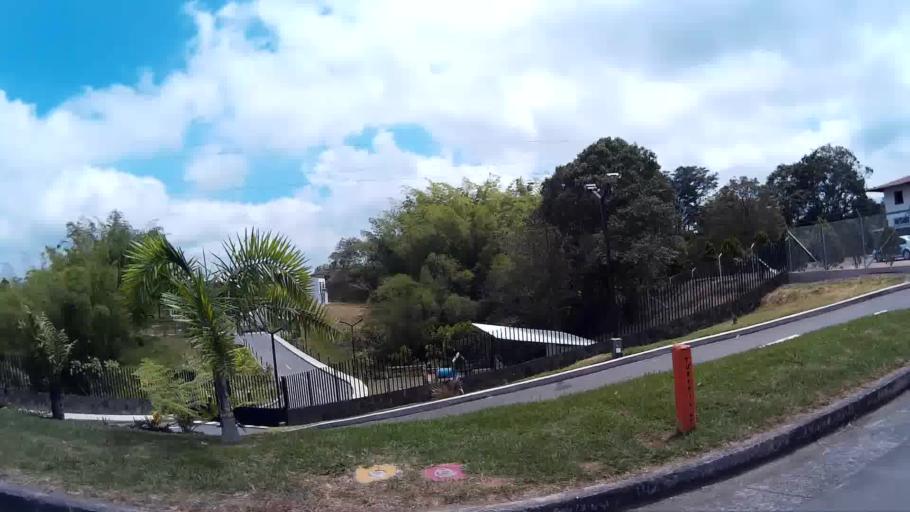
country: CO
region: Quindio
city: Circasia
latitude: 4.5897
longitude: -75.6420
